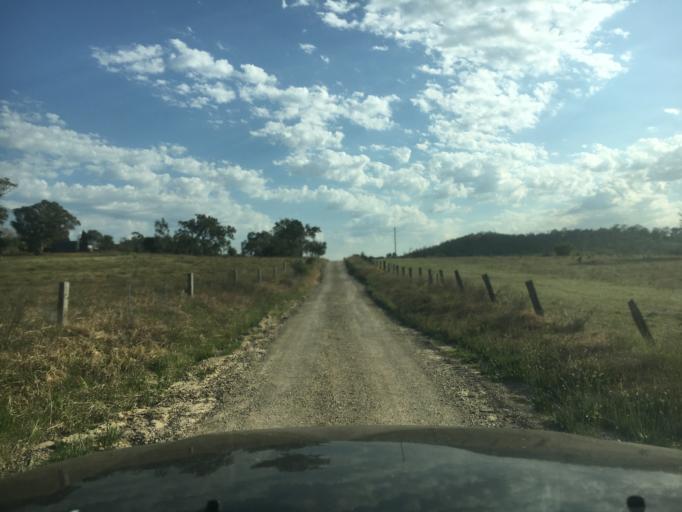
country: AU
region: New South Wales
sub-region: Cessnock
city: Branxton
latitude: -32.5988
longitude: 151.3440
